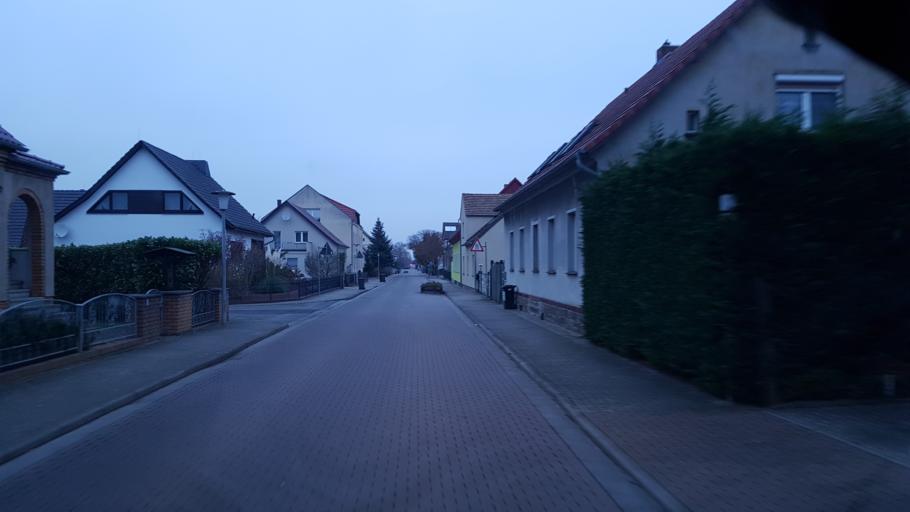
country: DE
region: Brandenburg
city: Vetschau
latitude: 51.7877
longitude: 14.0725
